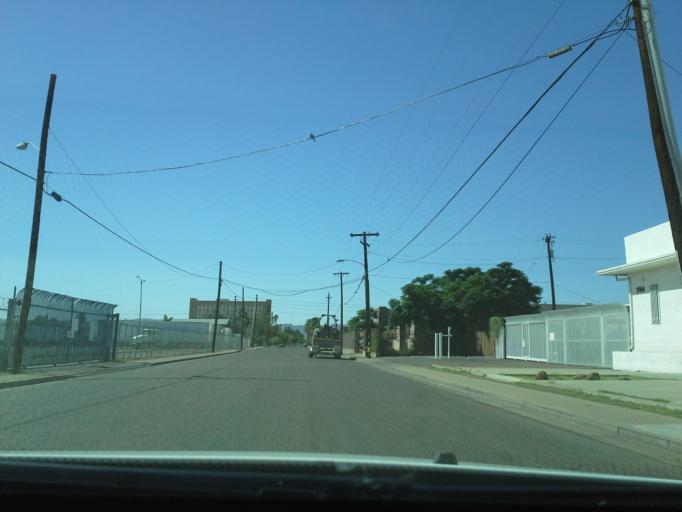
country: US
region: Arizona
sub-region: Maricopa County
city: Phoenix
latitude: 33.4564
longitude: -112.0957
